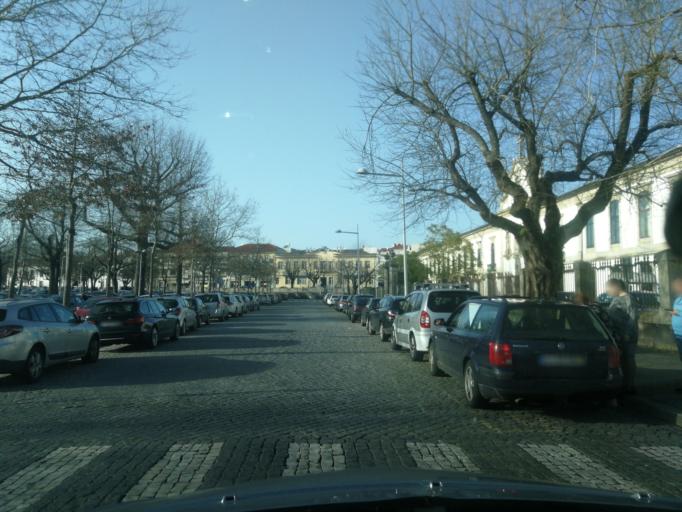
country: PT
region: Braga
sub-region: Barcelos
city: Barcelos
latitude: 41.5327
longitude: -8.6167
